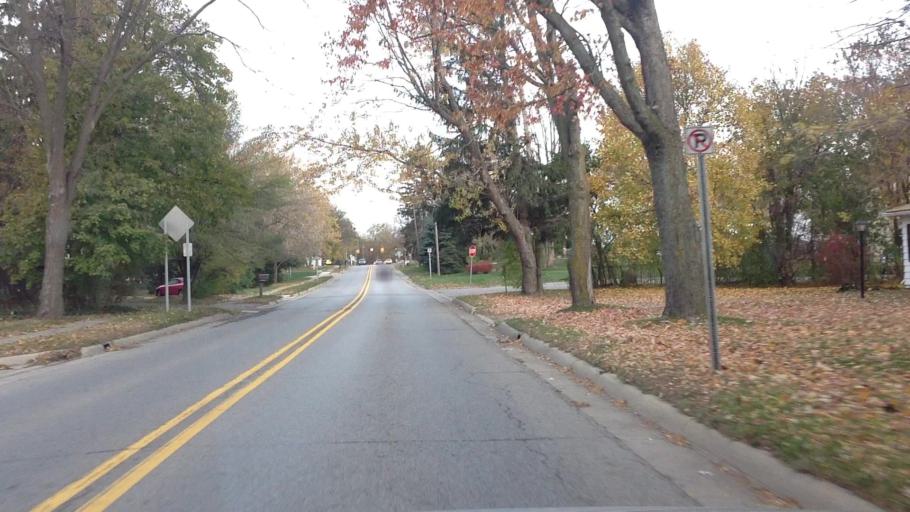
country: US
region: Michigan
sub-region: Oakland County
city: Sylvan Lake
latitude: 42.6319
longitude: -83.3367
